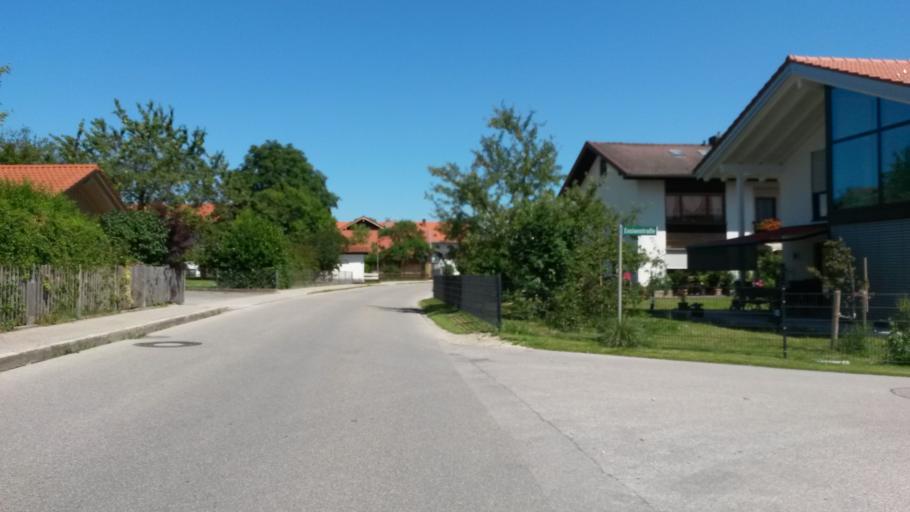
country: DE
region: Bavaria
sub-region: Upper Bavaria
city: Marquartstein
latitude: 47.7654
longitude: 12.4614
